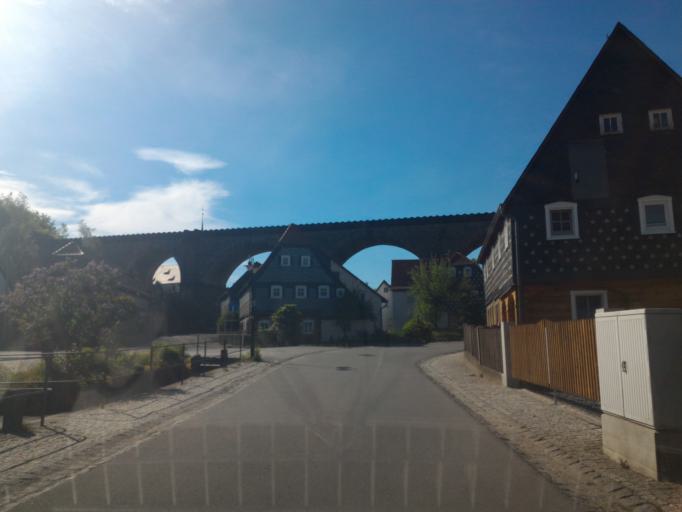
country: DE
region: Saxony
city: Niedercunnersdorf
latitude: 51.0376
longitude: 14.6668
